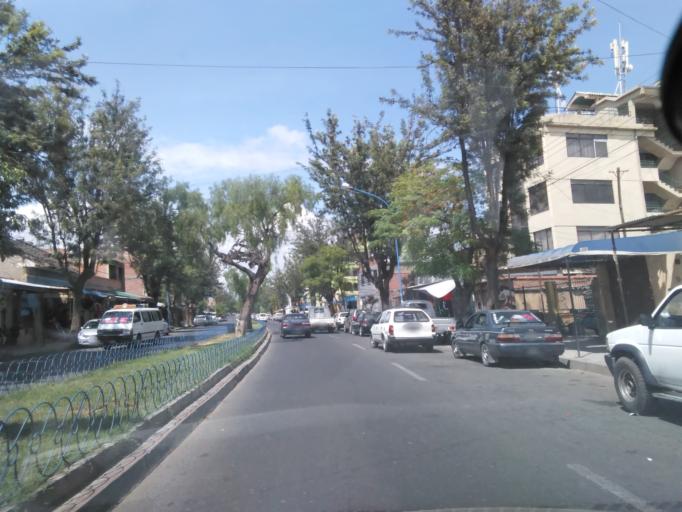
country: BO
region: Cochabamba
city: Cochabamba
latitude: -17.4042
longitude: -66.1633
